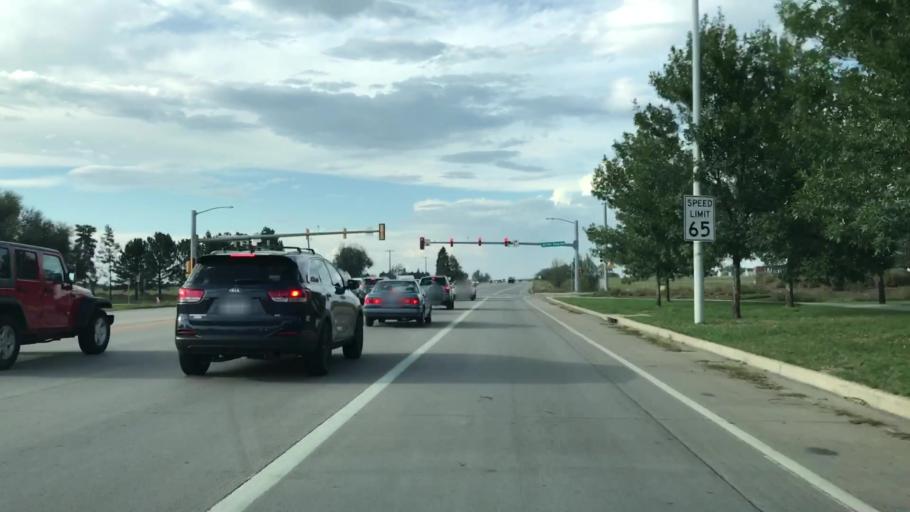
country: US
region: Colorado
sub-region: Boulder County
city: Longmont
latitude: 40.2054
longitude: -105.1024
